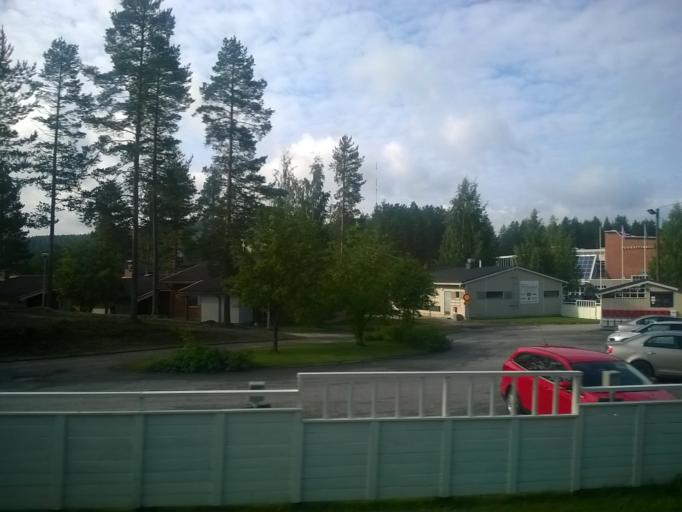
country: FI
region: Kainuu
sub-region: Kajaani
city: Vuokatti
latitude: 64.1400
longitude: 28.2892
